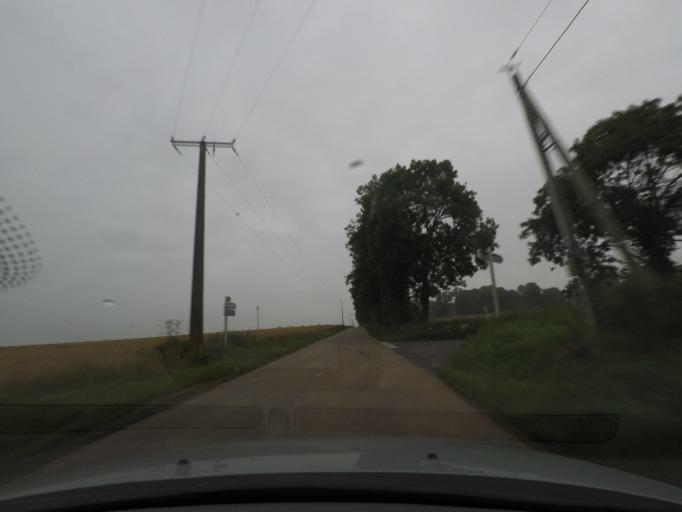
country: FR
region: Haute-Normandie
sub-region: Departement de la Seine-Maritime
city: Saint-Martin-Osmonville
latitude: 49.6019
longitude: 1.2438
